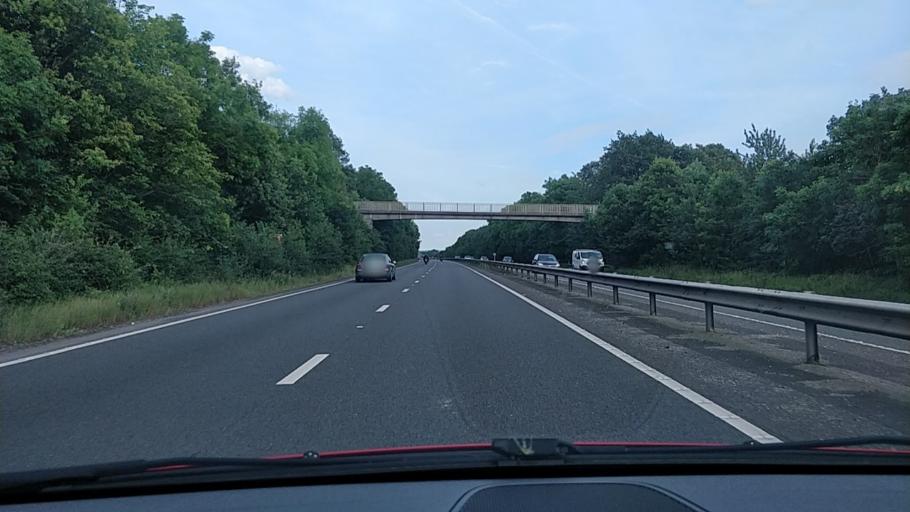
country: GB
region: Wales
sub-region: Wrexham
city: Rossett
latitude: 53.1614
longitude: -2.9598
